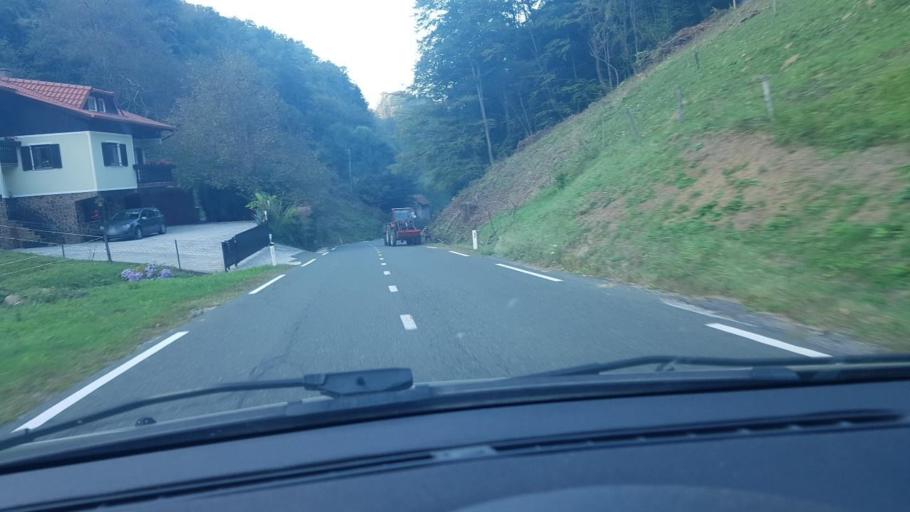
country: SI
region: Rogatec
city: Rogatec
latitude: 46.2697
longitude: 15.7126
